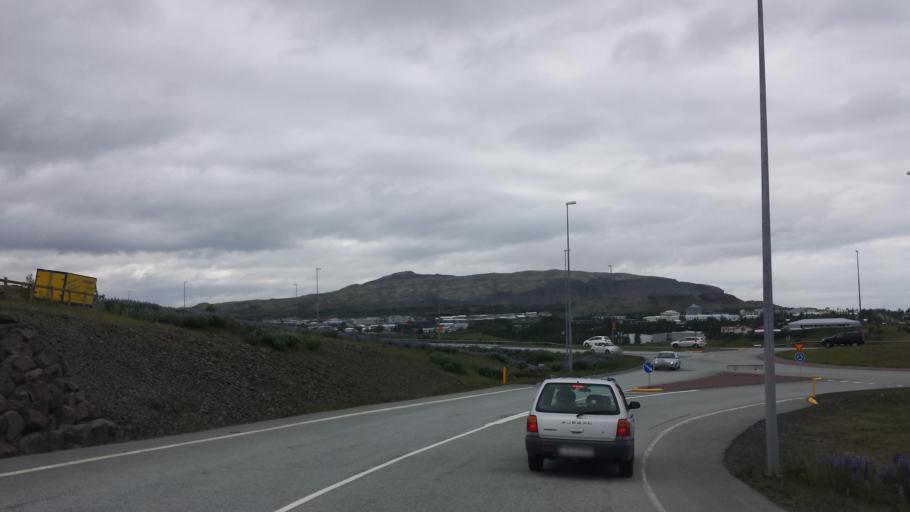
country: IS
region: Capital Region
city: Mosfellsbaer
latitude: 64.1764
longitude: -21.6754
